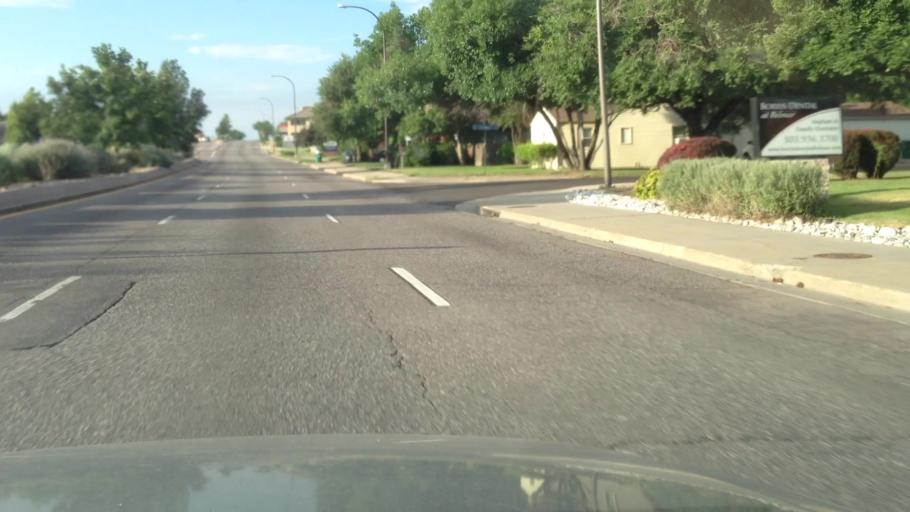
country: US
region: Colorado
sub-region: Jefferson County
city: Lakewood
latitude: 39.7170
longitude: -105.0817
